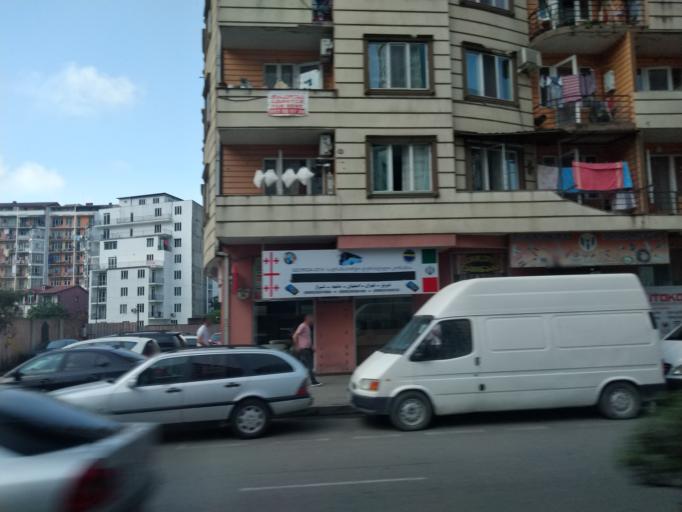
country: GE
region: Ajaria
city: Batumi
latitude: 41.6335
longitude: 41.6105
